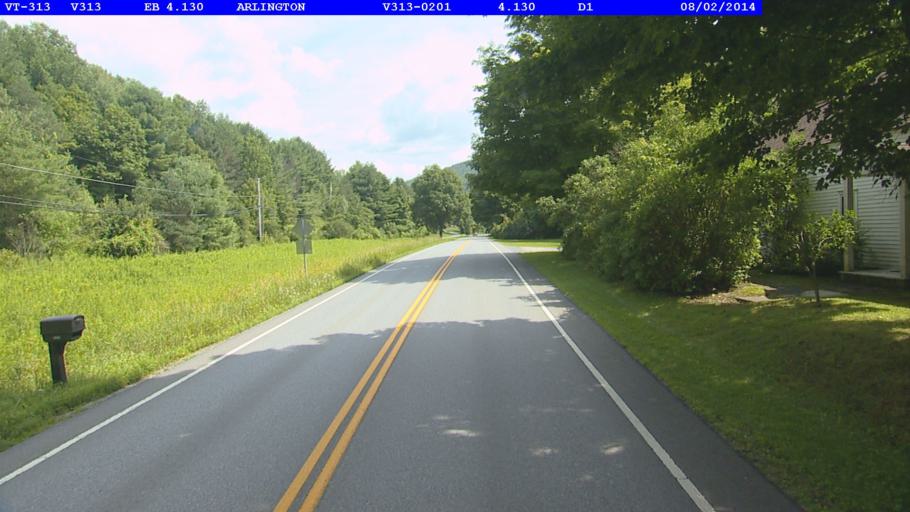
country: US
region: Vermont
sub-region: Bennington County
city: Arlington
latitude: 43.0898
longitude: -73.1952
